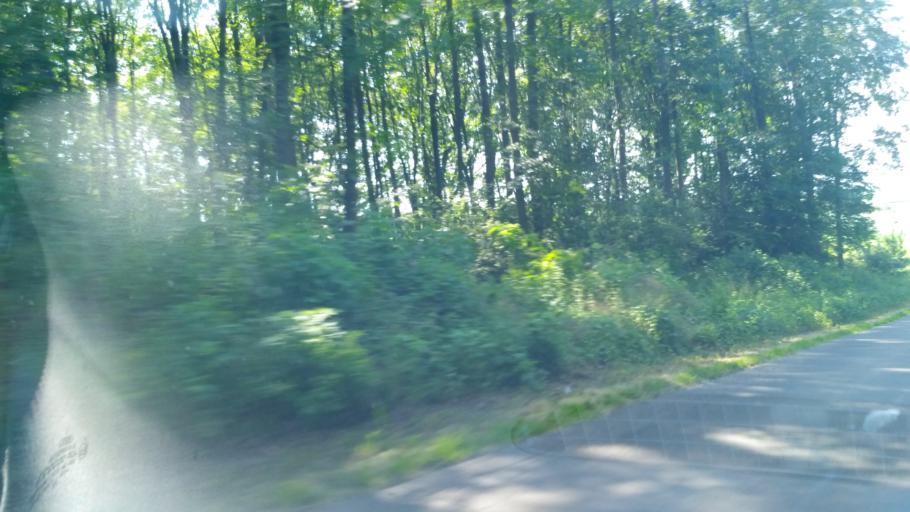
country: PL
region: Subcarpathian Voivodeship
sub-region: Powiat jaroslawski
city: Rokietnica
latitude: 49.9304
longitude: 22.6755
